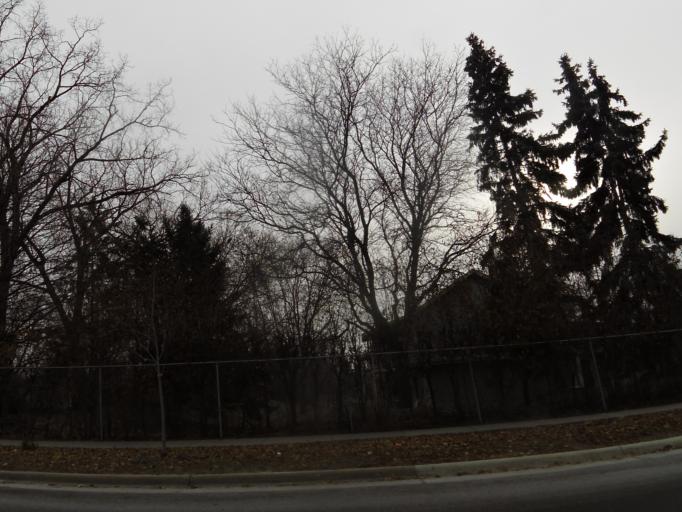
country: US
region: Minnesota
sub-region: Ramsey County
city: Maplewood
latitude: 44.9568
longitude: -93.0404
